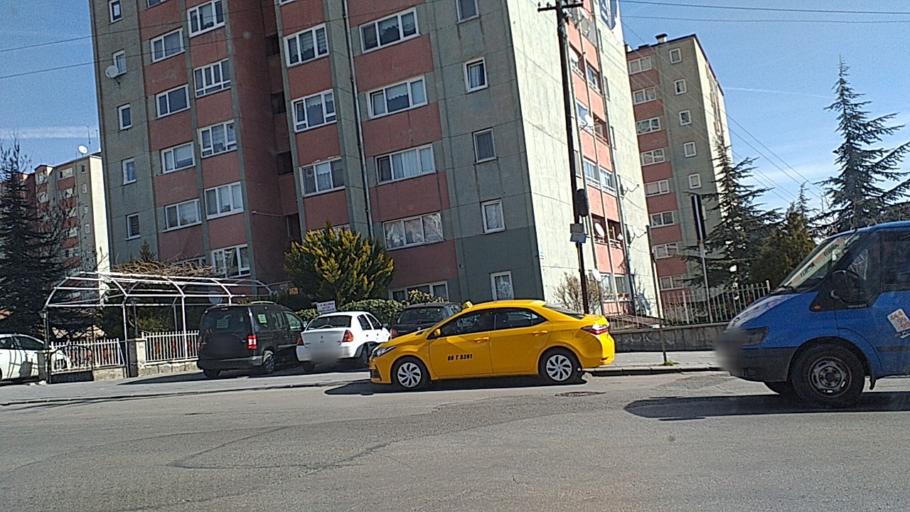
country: TR
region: Ankara
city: Ankara
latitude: 39.9820
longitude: 32.8355
